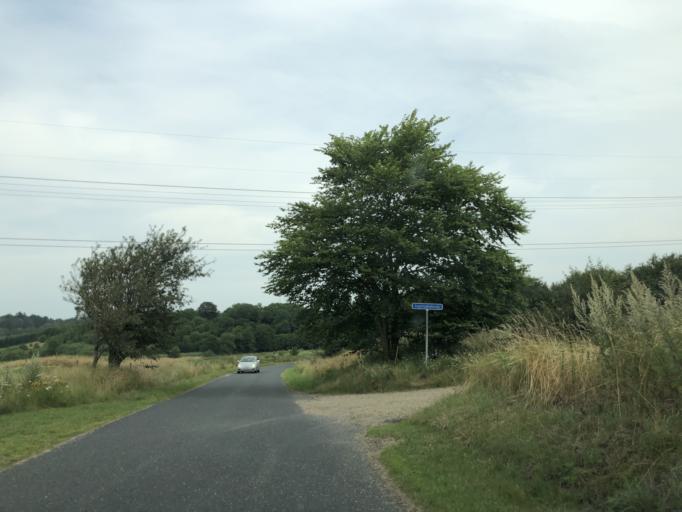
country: DK
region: Central Jutland
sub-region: Viborg Kommune
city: Viborg
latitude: 56.4884
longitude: 9.5190
